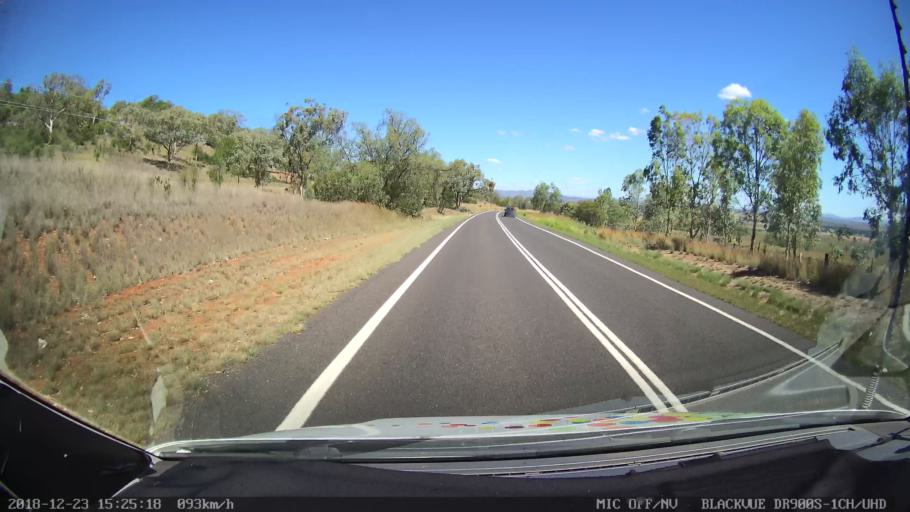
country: AU
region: New South Wales
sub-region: Tamworth Municipality
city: Manilla
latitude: -30.9022
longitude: 150.8297
